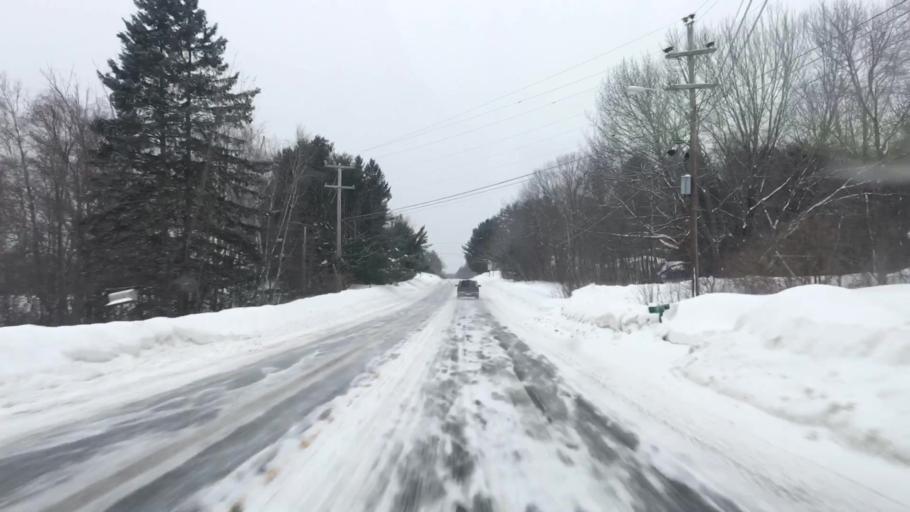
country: US
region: Maine
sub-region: Penobscot County
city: Medway
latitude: 45.5960
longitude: -68.4951
